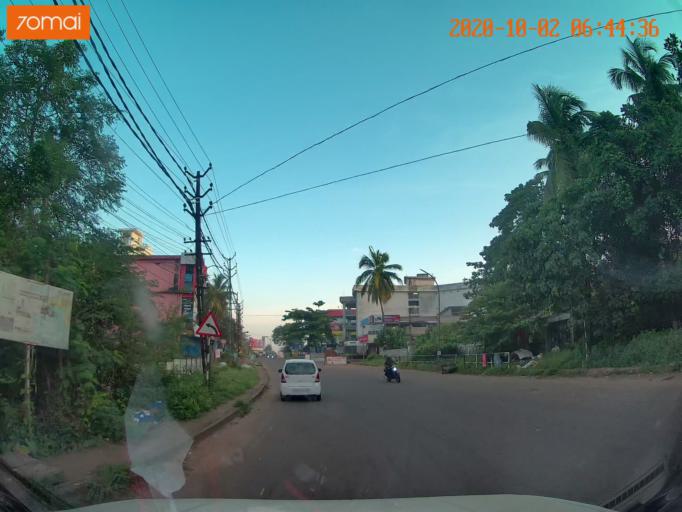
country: IN
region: Kerala
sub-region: Malappuram
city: Ponnani
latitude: 10.7864
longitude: 76.0085
